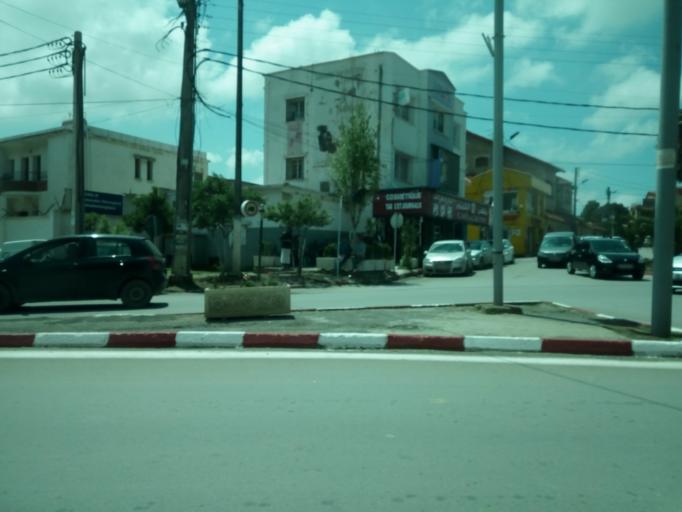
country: DZ
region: Tipaza
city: Saoula
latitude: 36.7200
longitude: 2.9953
